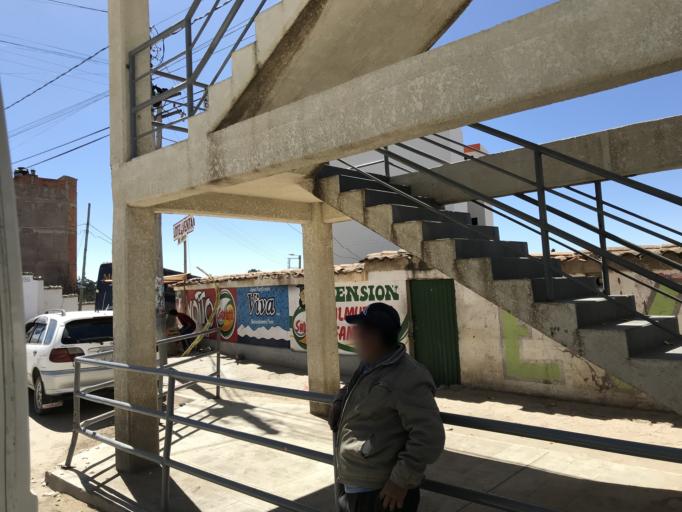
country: BO
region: Chuquisaca
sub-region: Provincia Oropeza
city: Huata
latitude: -19.0208
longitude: -65.2486
